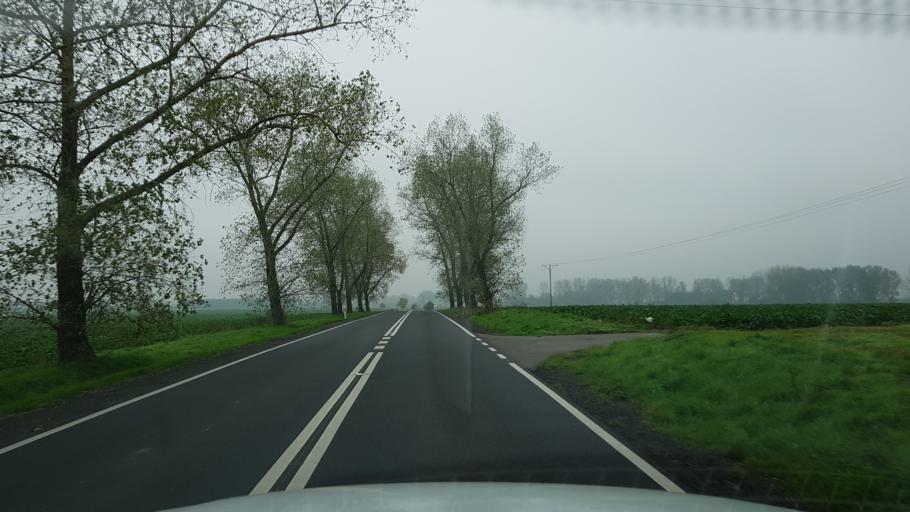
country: PL
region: West Pomeranian Voivodeship
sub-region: Powiat stargardzki
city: Stargard Szczecinski
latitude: 53.2501
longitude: 15.1026
